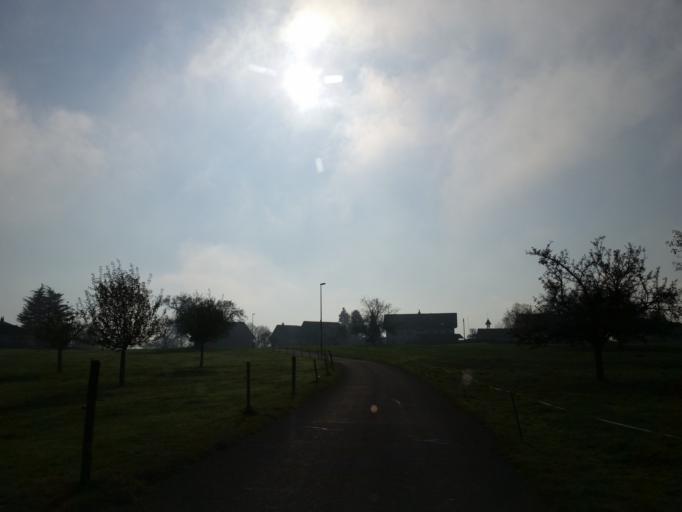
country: CH
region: Thurgau
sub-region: Arbon District
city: Arbon
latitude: 47.5297
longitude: 9.4077
